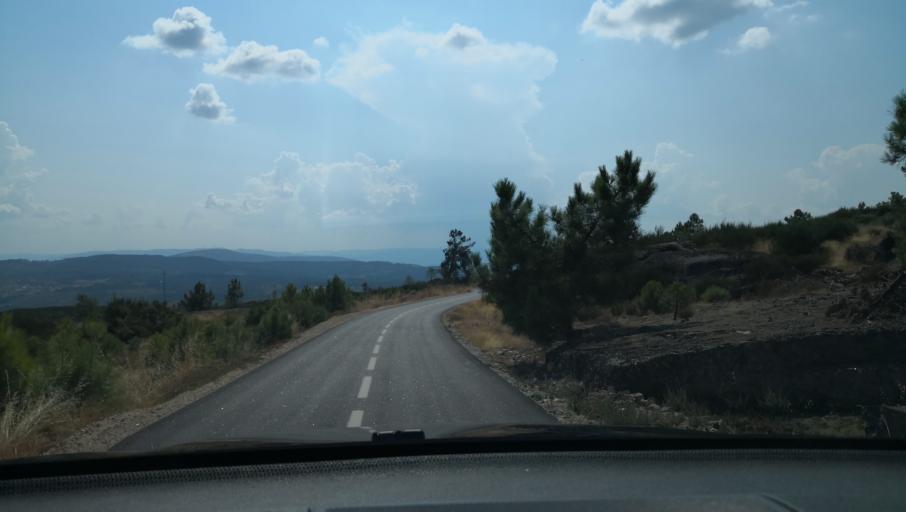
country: PT
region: Vila Real
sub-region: Sabrosa
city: Sabrosa
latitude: 41.2828
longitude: -7.6144
